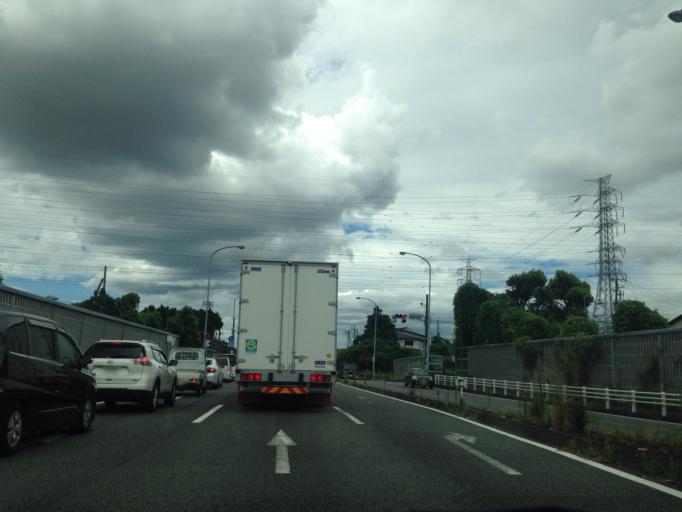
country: JP
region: Shizuoka
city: Mishima
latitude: 35.1382
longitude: 138.8827
